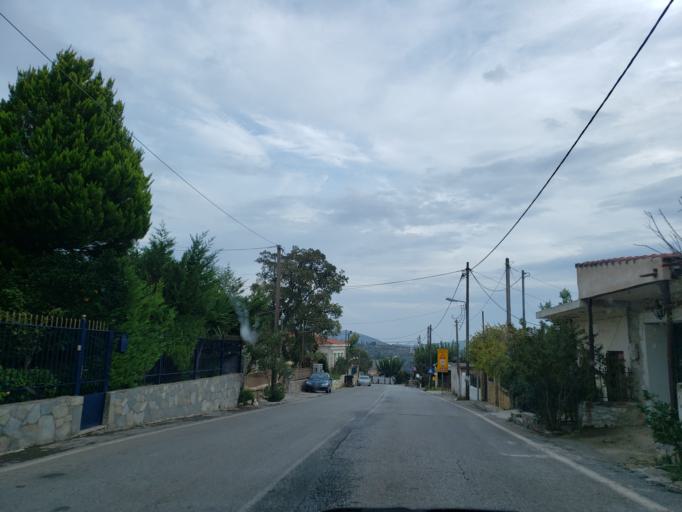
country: GR
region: Attica
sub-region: Nomarchia Anatolikis Attikis
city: Grammatiko
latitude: 38.2032
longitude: 23.9655
